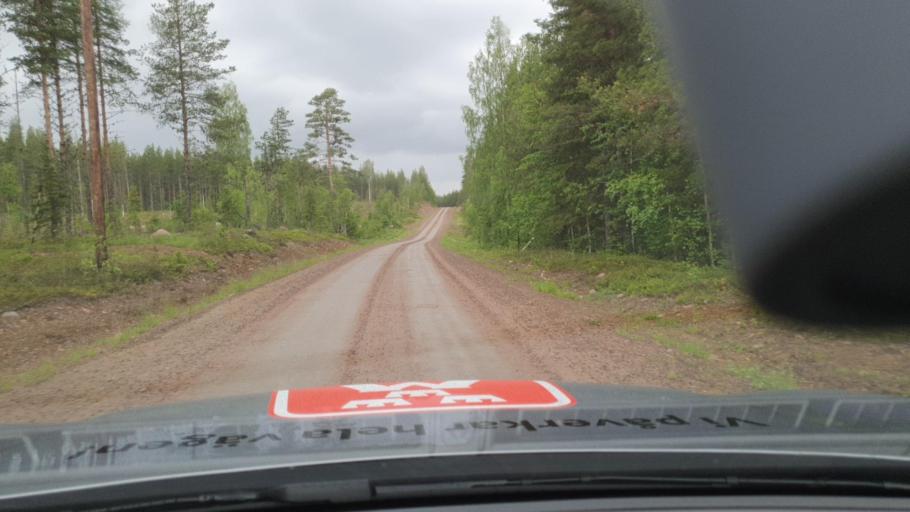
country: SE
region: Norrbotten
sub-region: Overkalix Kommun
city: OEverkalix
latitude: 66.6314
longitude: 22.7169
